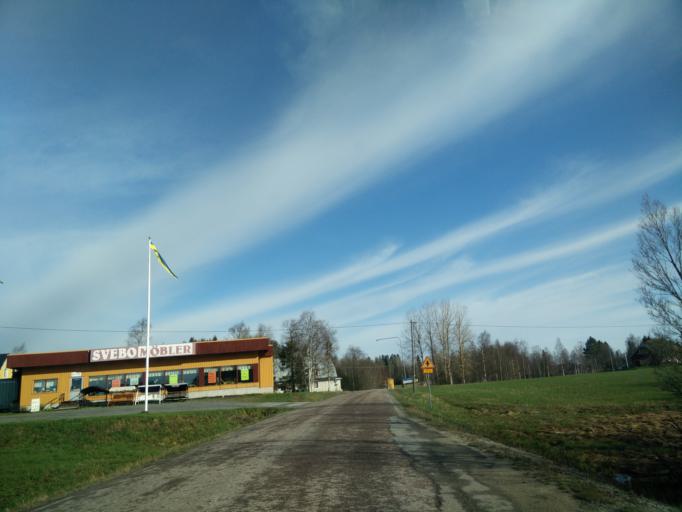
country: SE
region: Vaesternorrland
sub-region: Haernoesands Kommun
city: Haernoesand
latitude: 62.5887
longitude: 17.7879
